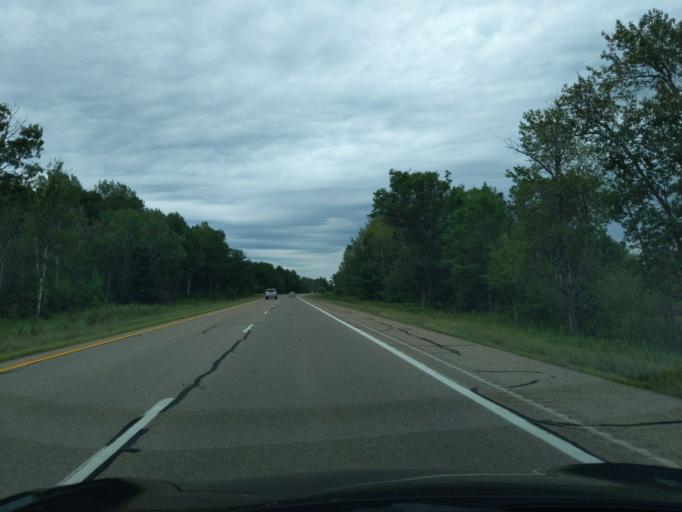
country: US
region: Michigan
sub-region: Roscommon County
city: Houghton Lake
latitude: 44.2804
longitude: -84.8005
